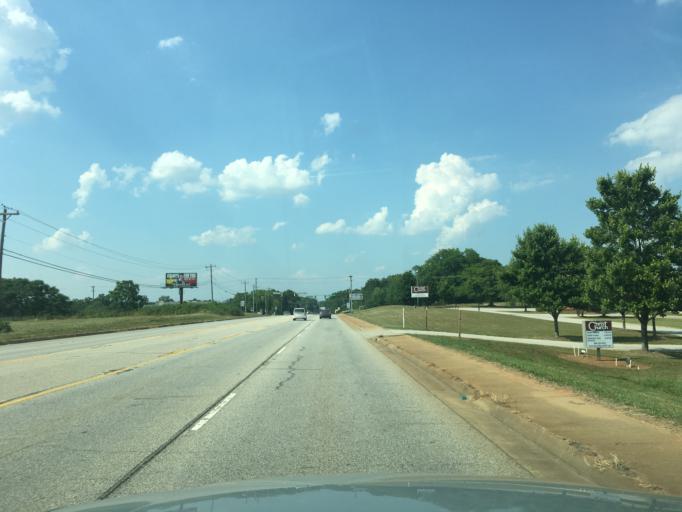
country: US
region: South Carolina
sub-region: Anderson County
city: Northlake
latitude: 34.5751
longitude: -82.6233
